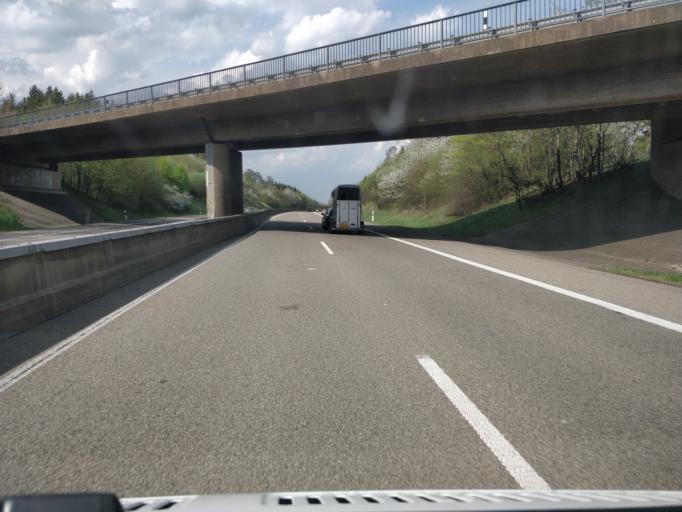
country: DE
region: North Rhine-Westphalia
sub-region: Regierungsbezirk Koln
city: Nettersheim
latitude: 50.5054
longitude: 6.6639
